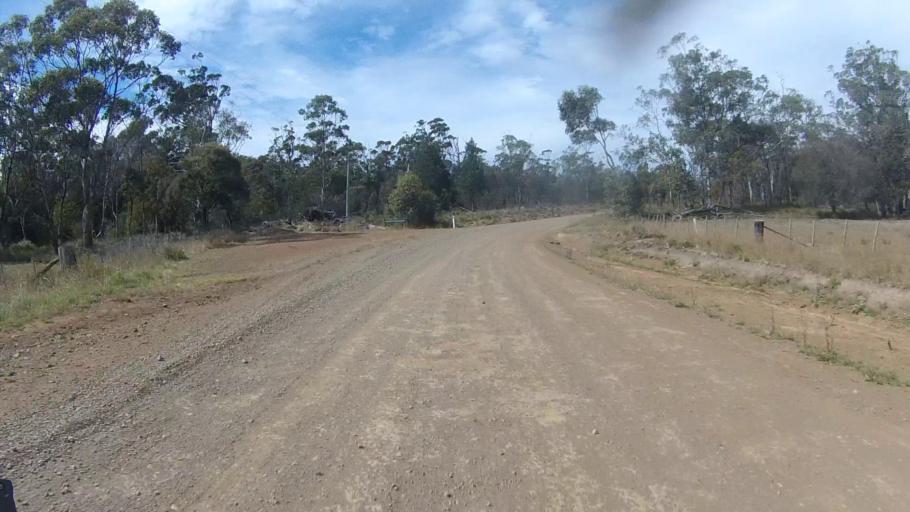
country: AU
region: Tasmania
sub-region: Sorell
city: Sorell
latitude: -42.6481
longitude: 147.8995
